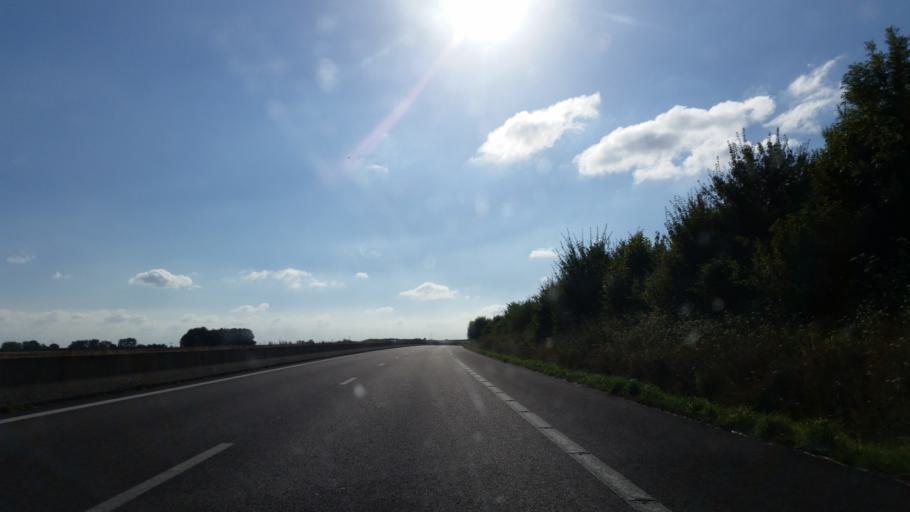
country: FR
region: Haute-Normandie
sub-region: Departement de la Seine-Maritime
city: Gaillefontaine
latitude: 49.7386
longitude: 1.6288
